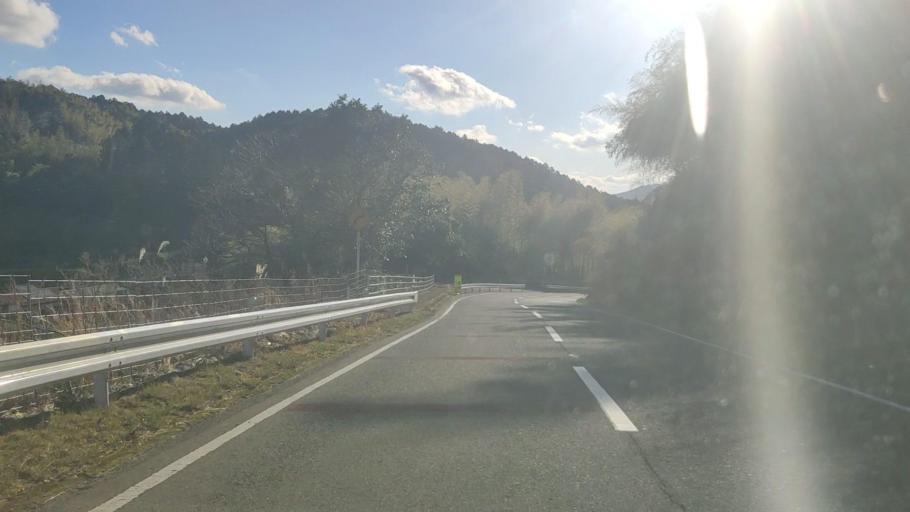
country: JP
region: Saga Prefecture
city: Kanzakimachi-kanzaki
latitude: 33.3904
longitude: 130.2662
